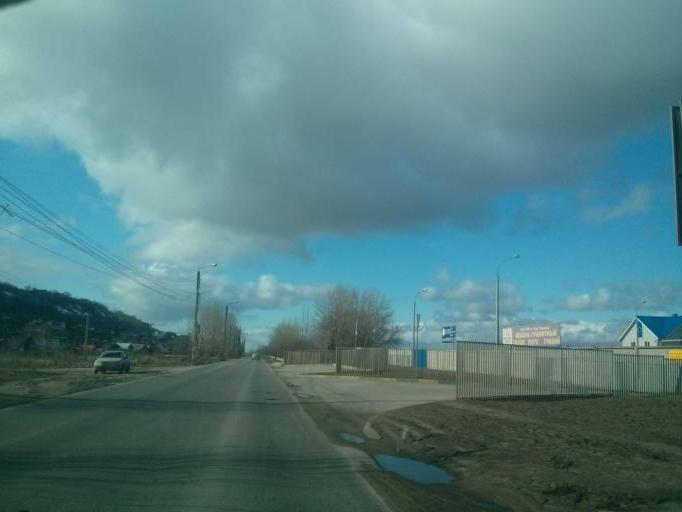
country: RU
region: Nizjnij Novgorod
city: Afonino
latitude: 56.2996
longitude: 44.1039
